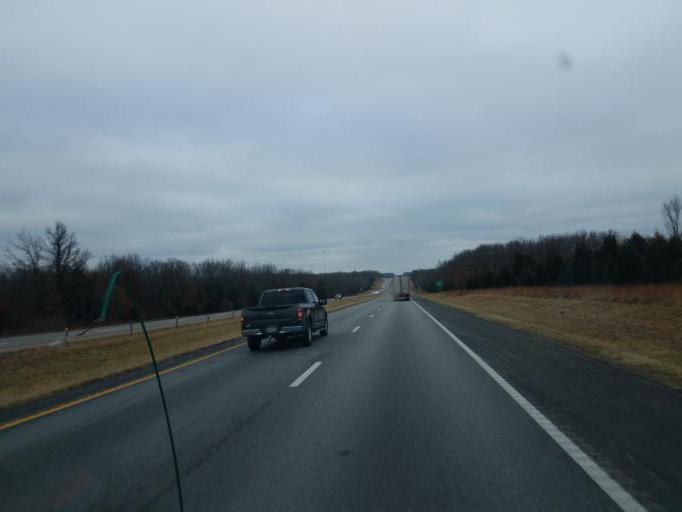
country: US
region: Missouri
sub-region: Webster County
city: Marshfield
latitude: 37.4855
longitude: -92.8515
